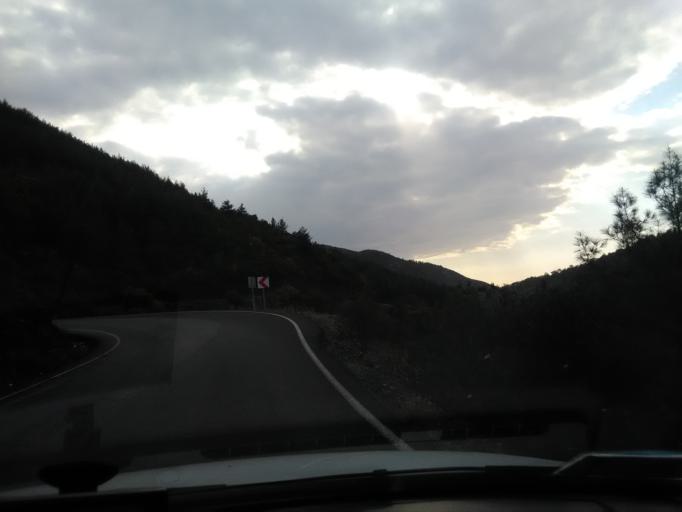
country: TR
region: Antalya
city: Gazipasa
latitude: 36.2962
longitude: 32.3806
